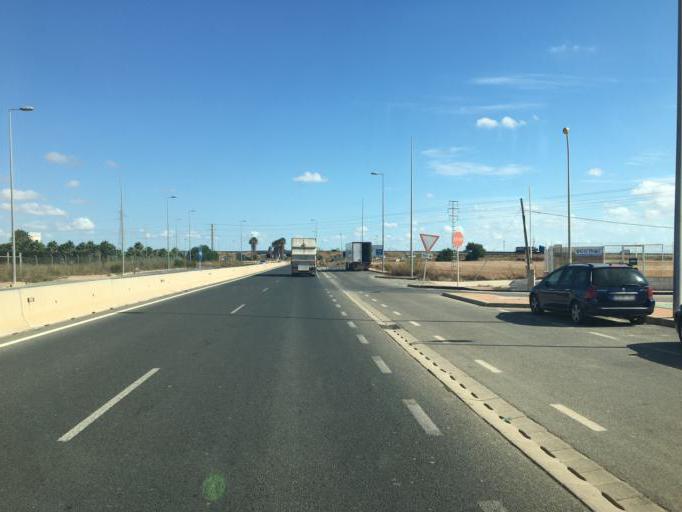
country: ES
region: Murcia
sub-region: Murcia
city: Cartagena
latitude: 37.6542
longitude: -0.9824
